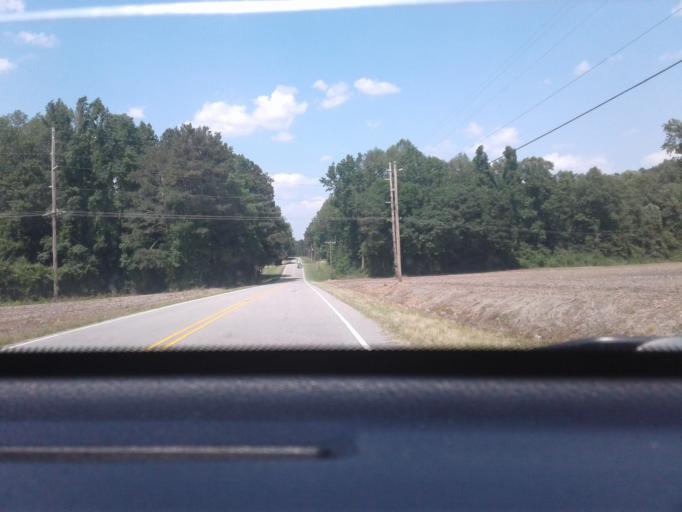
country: US
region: North Carolina
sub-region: Cumberland County
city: Eastover
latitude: 35.1806
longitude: -78.7097
